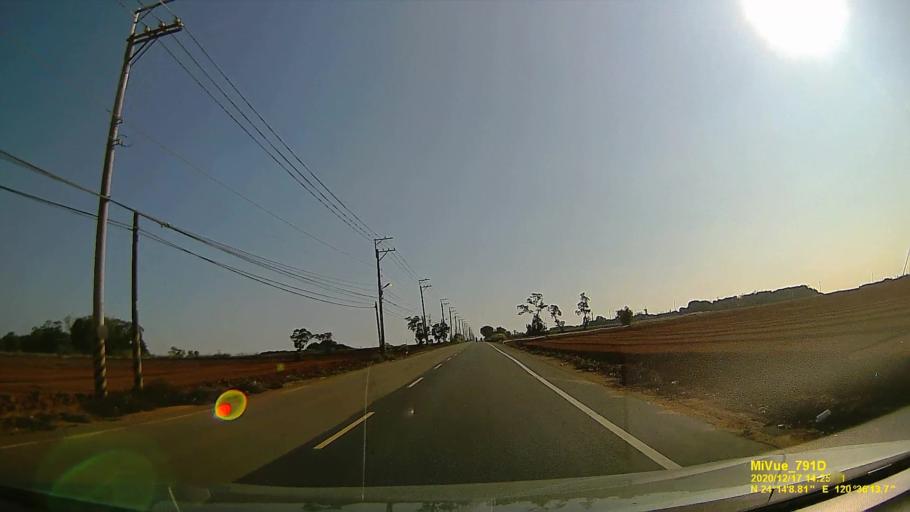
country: TW
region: Taiwan
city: Fengyuan
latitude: 24.2358
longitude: 120.6038
